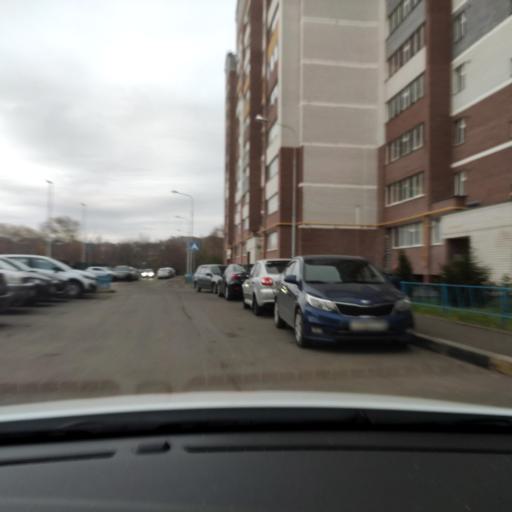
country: RU
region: Tatarstan
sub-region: Gorod Kazan'
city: Kazan
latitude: 55.8045
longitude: 49.2125
